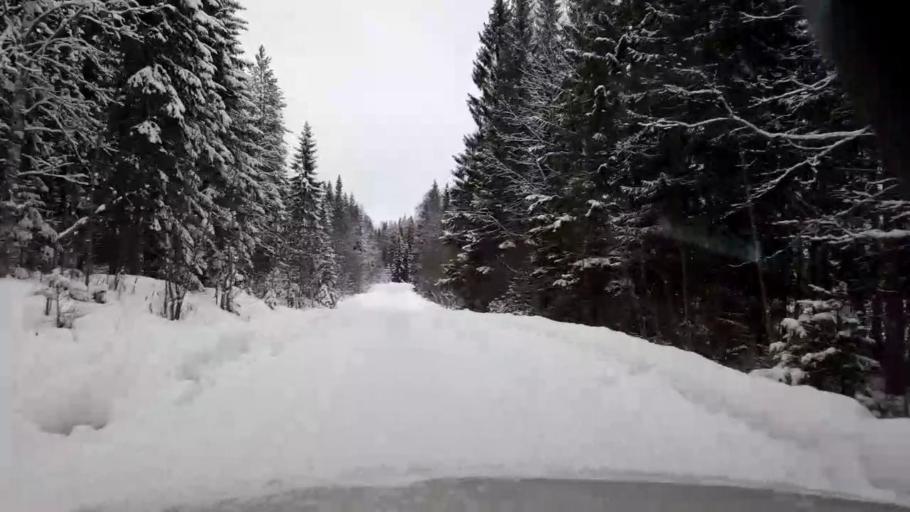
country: SE
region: Vaesternorrland
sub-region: Ange Kommun
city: Ange
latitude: 62.2333
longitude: 15.3924
